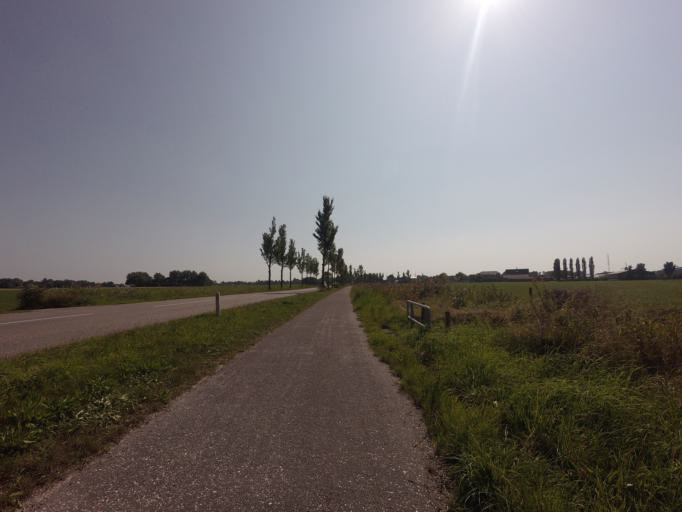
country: NL
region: Groningen
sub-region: Gemeente Zuidhorn
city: Grijpskerk
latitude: 53.2714
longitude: 6.3068
